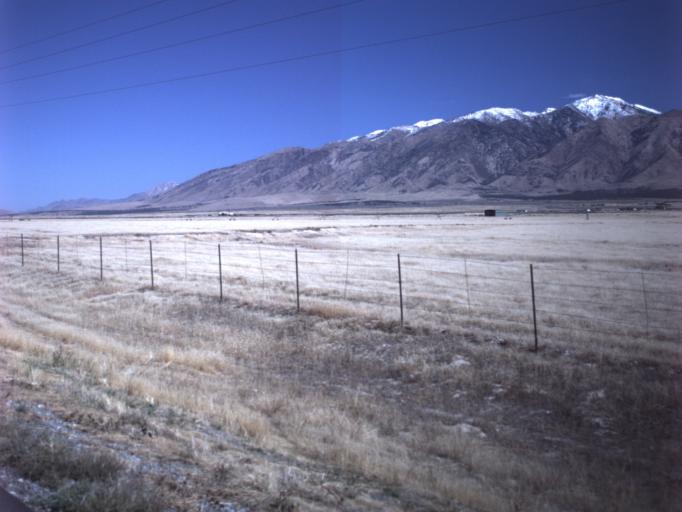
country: US
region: Utah
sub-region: Tooele County
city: Grantsville
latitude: 40.3849
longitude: -112.7471
